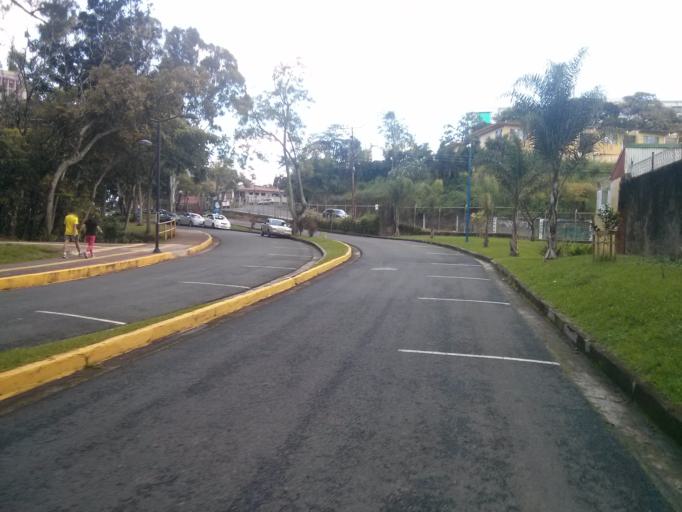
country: CR
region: San Jose
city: San Pedro
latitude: 9.9370
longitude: -84.0477
